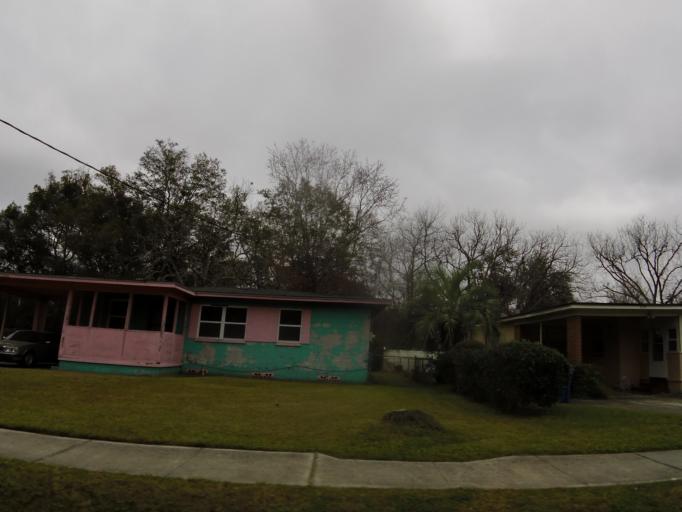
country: US
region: Florida
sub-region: Duval County
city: Jacksonville
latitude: 30.3703
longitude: -81.7129
